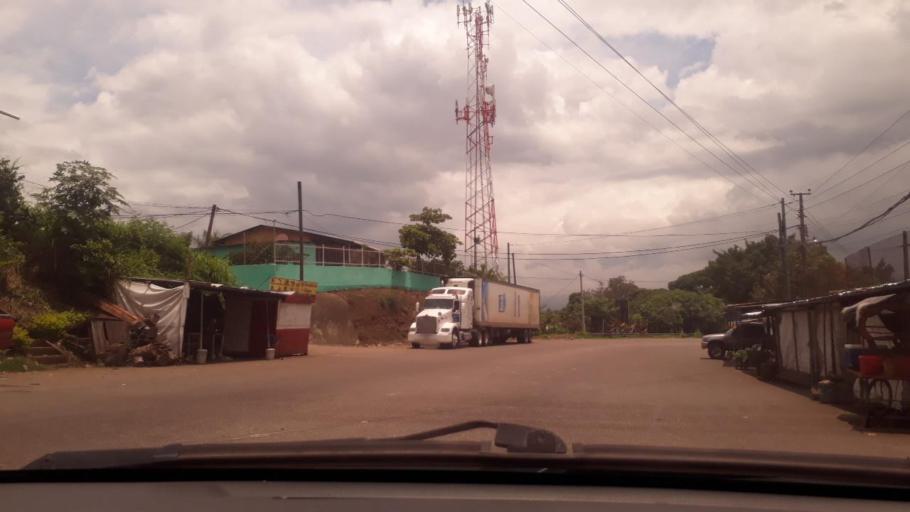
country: GT
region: Santa Rosa
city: Cuilapa
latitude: 14.2513
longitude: -90.2771
